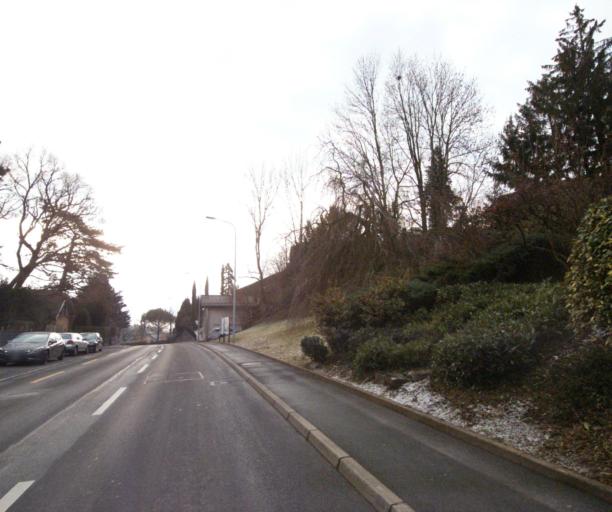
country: CH
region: Vaud
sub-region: Riviera-Pays-d'Enhaut District
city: La Tour-de-Peilz
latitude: 46.4532
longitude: 6.8685
